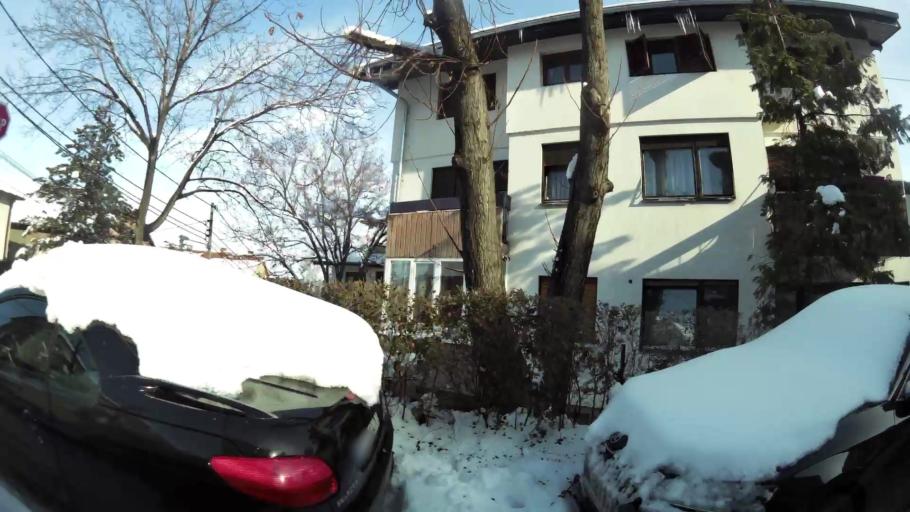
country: RS
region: Central Serbia
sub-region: Belgrade
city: Palilula
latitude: 44.8065
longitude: 20.5196
